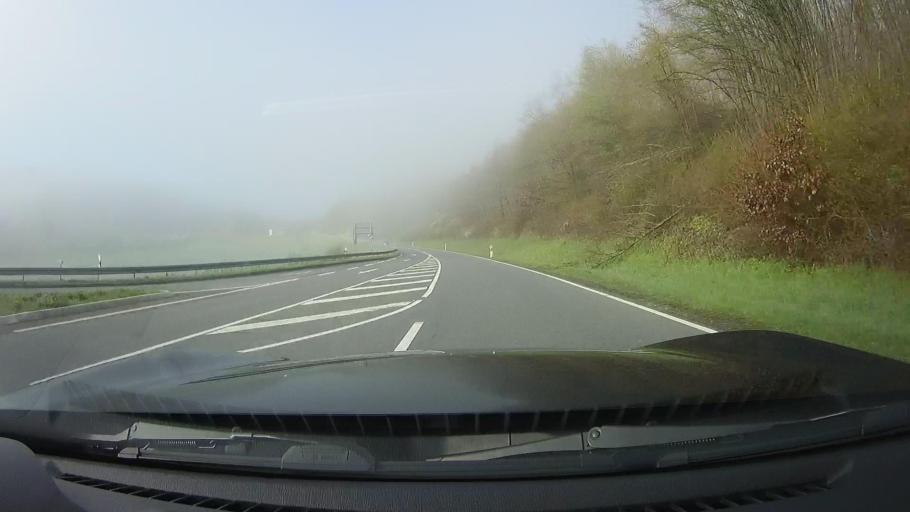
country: DE
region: Baden-Wuerttemberg
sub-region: Karlsruhe Region
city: Adelsheim
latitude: 49.4190
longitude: 9.4021
